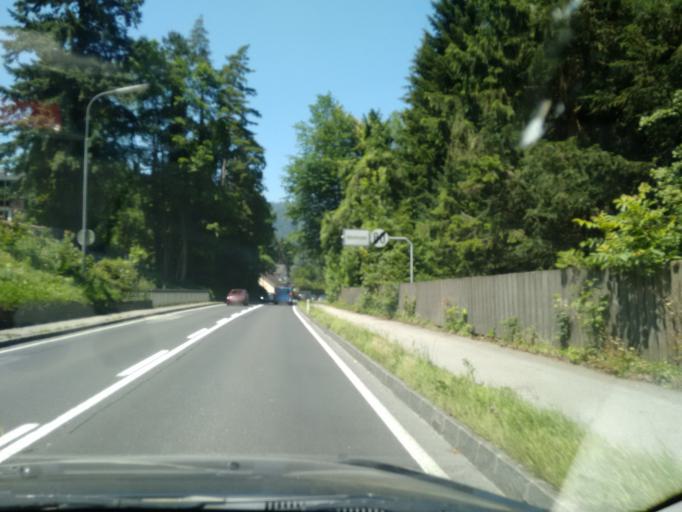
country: AT
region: Upper Austria
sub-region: Politischer Bezirk Gmunden
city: Altmunster
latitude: 47.8907
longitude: 13.7679
